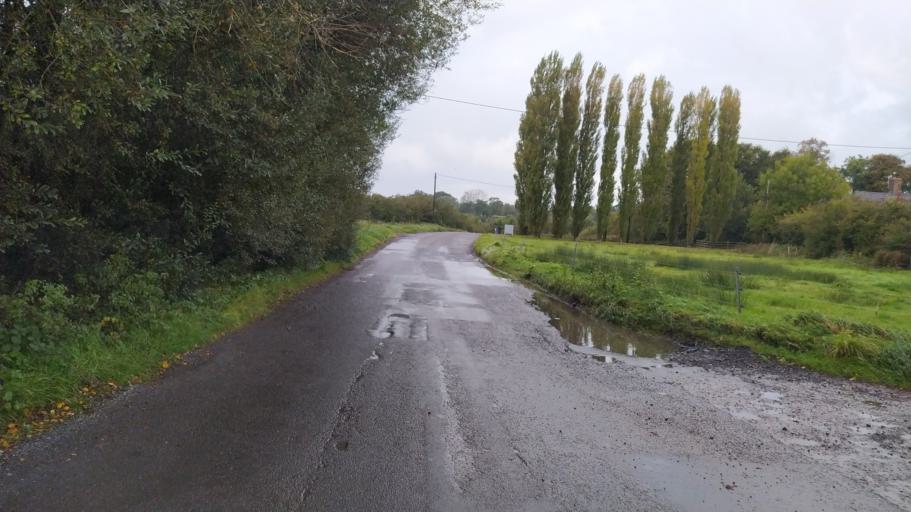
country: GB
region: England
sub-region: Dorset
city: Shaftesbury
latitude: 51.0453
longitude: -2.1815
